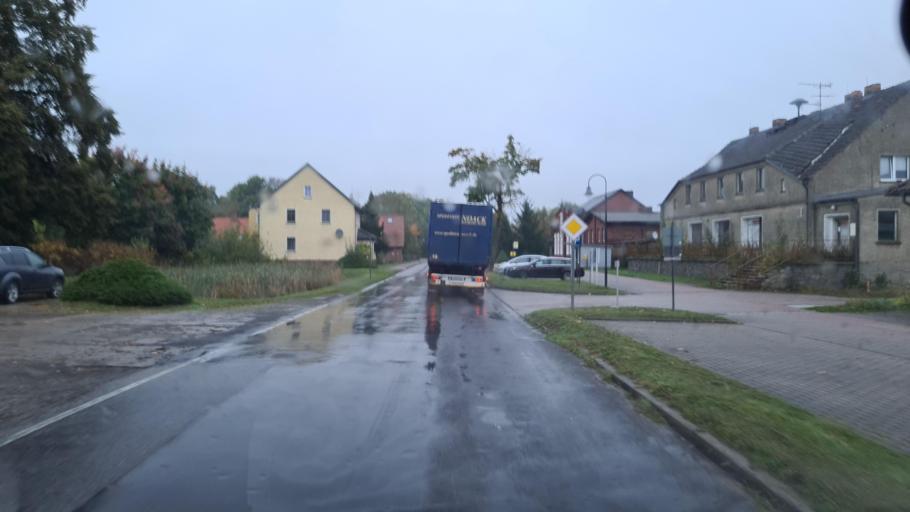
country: DE
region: Brandenburg
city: Rietz Neuendorf
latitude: 52.2639
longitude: 14.1618
